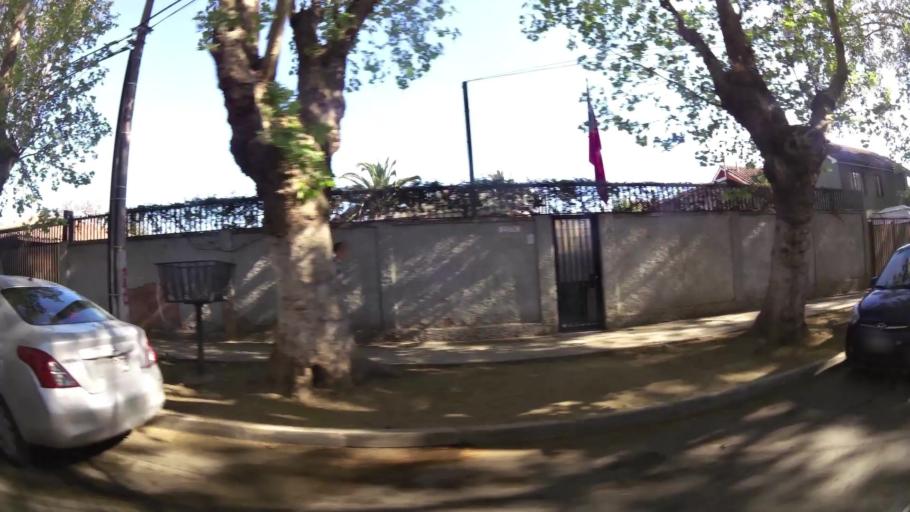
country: CL
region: Santiago Metropolitan
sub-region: Provincia de Talagante
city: Penaflor
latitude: -33.5987
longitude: -70.8754
